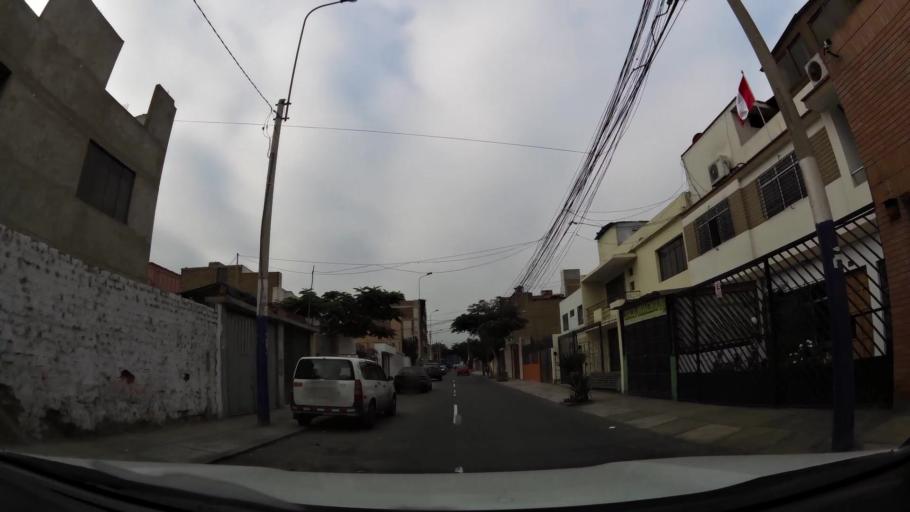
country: PE
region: Lima
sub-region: Lima
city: Surco
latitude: -12.1697
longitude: -77.0208
